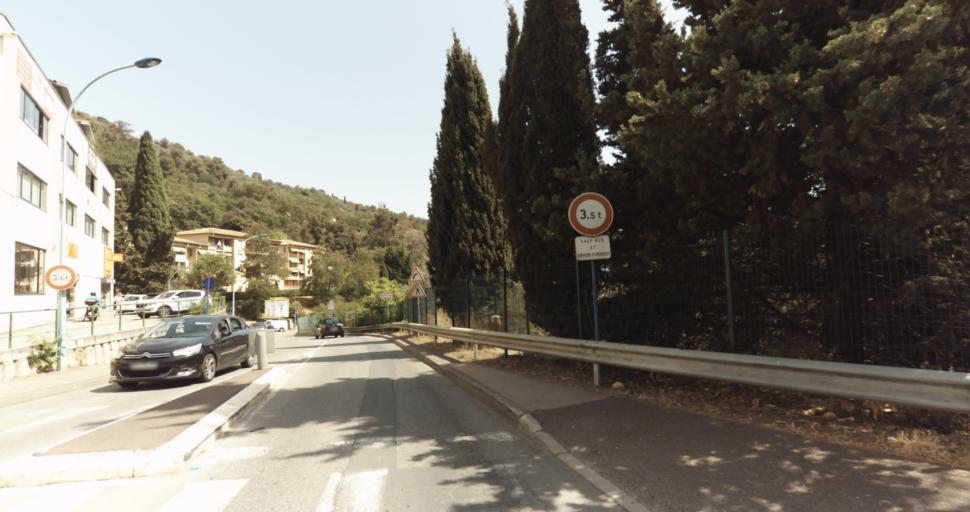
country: FR
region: Provence-Alpes-Cote d'Azur
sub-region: Departement des Alpes-Maritimes
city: Sainte-Agnes
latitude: 43.8033
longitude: 7.4879
